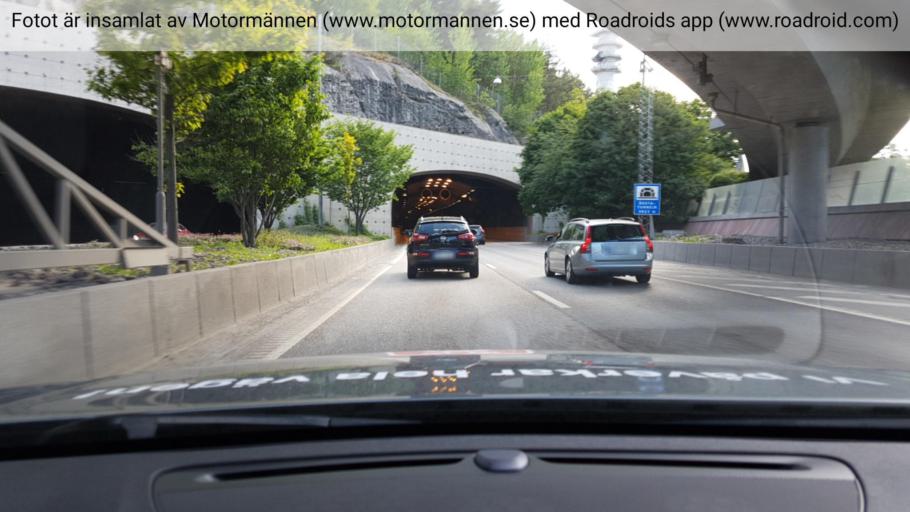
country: SE
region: Stockholm
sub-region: Stockholms Kommun
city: OEstermalm
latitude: 59.3005
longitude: 18.1074
